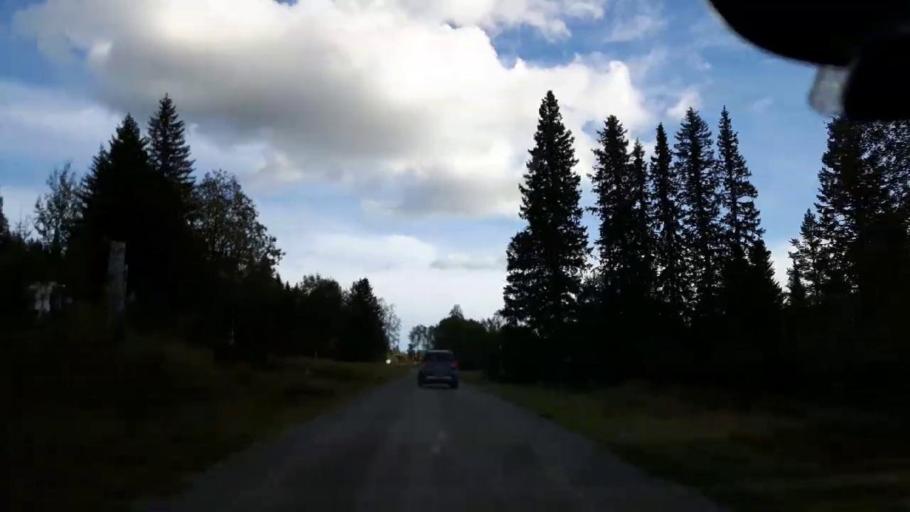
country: SE
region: Jaemtland
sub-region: Ragunda Kommun
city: Hammarstrand
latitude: 63.4143
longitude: 16.0808
